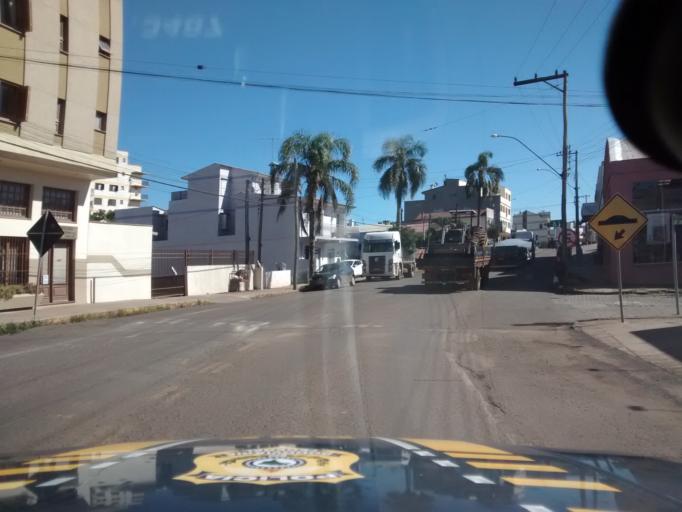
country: BR
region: Rio Grande do Sul
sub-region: Vacaria
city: Vacaria
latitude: -28.5104
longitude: -50.9341
